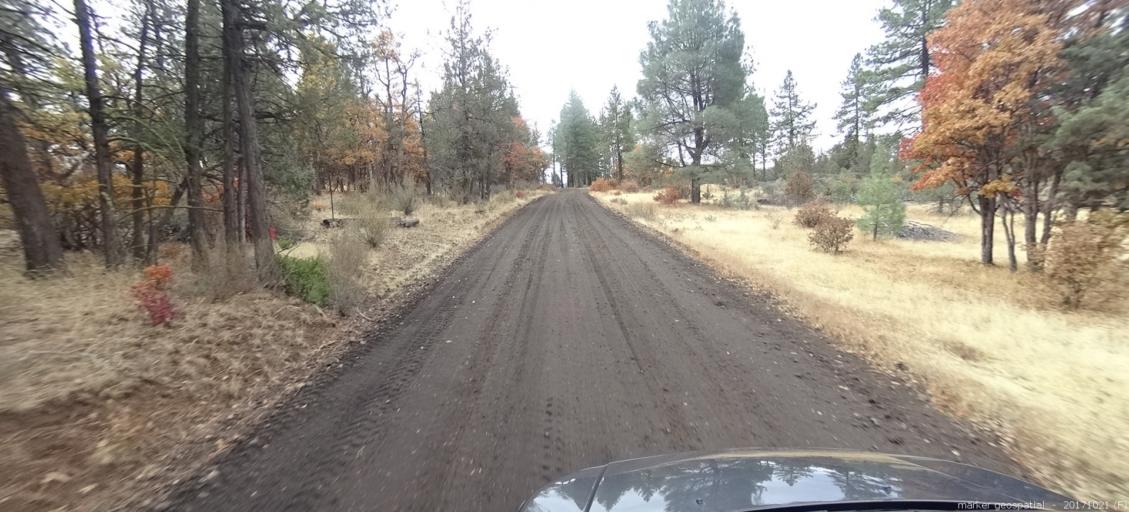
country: US
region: California
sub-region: Shasta County
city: Burney
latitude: 40.9419
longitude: -121.4411
